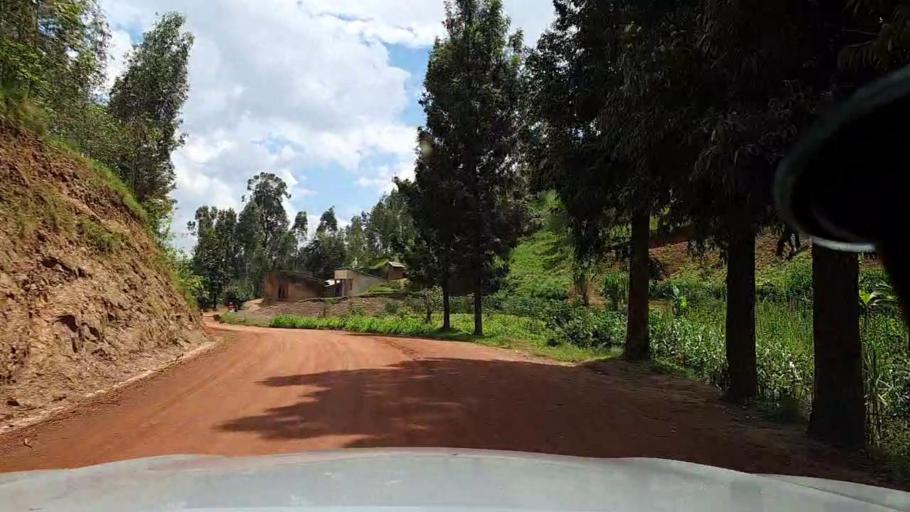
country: RW
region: Northern Province
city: Byumba
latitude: -1.7539
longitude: 29.8500
